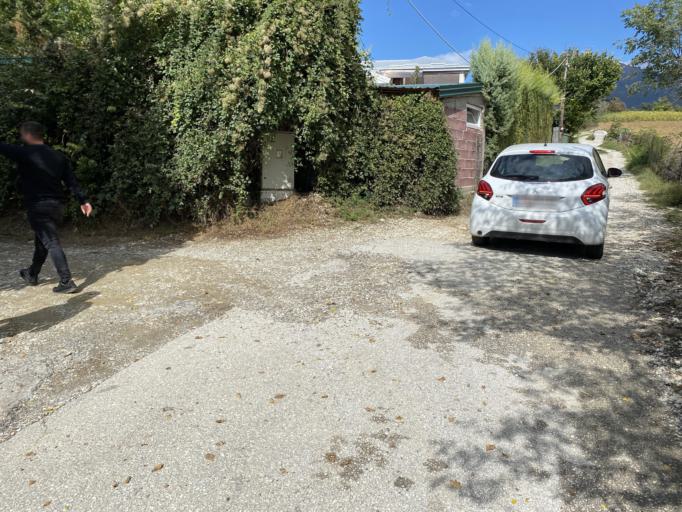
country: MK
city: Radishani
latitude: 42.0824
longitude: 21.4530
